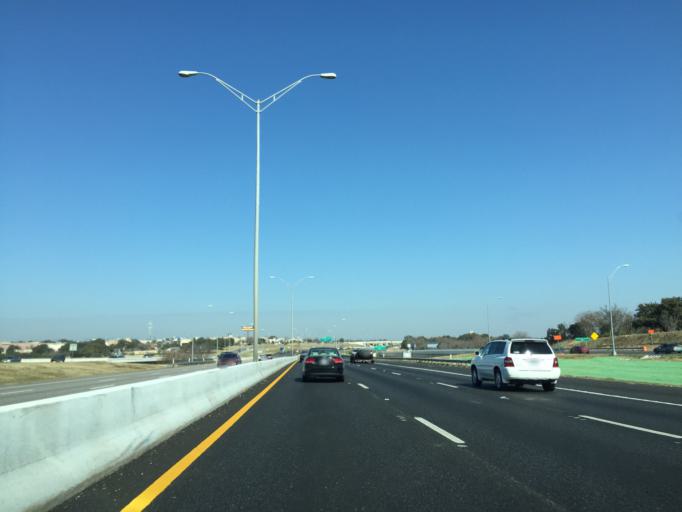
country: US
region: Texas
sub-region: Williamson County
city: Georgetown
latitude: 30.6240
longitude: -97.6906
